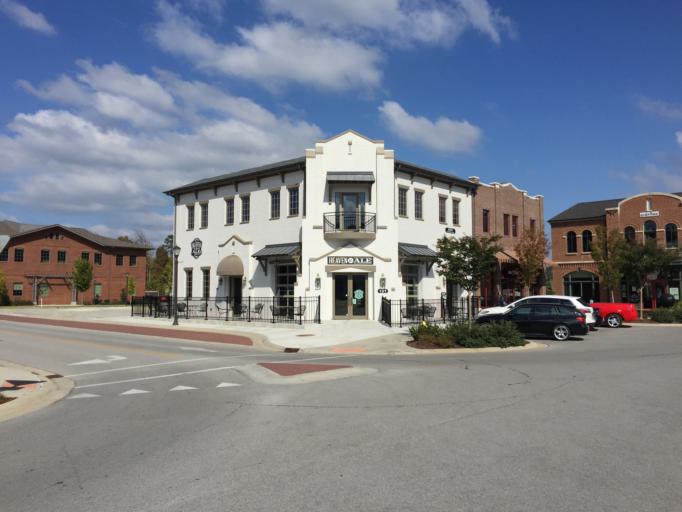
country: US
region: Tennessee
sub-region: Hamilton County
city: Collegedale
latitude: 35.0829
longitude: -85.0555
